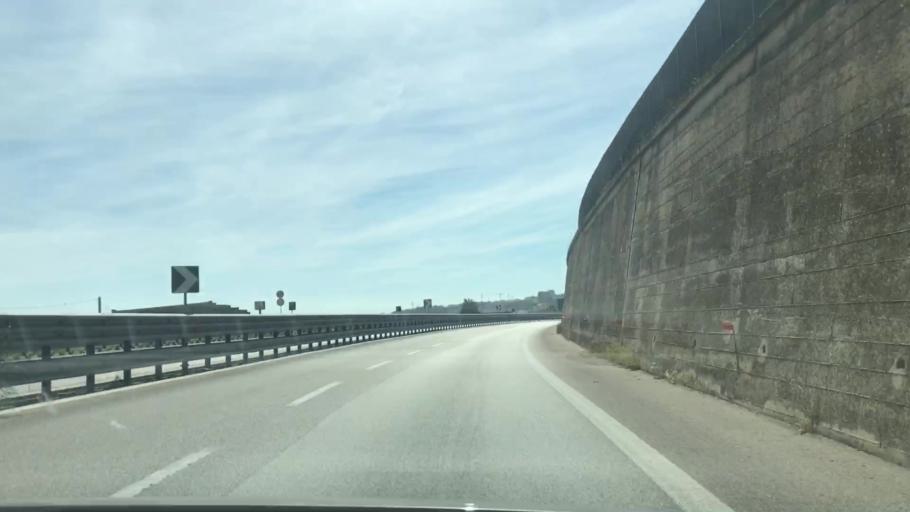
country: IT
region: Basilicate
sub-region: Provincia di Matera
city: Matera
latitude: 40.6958
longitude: 16.5909
